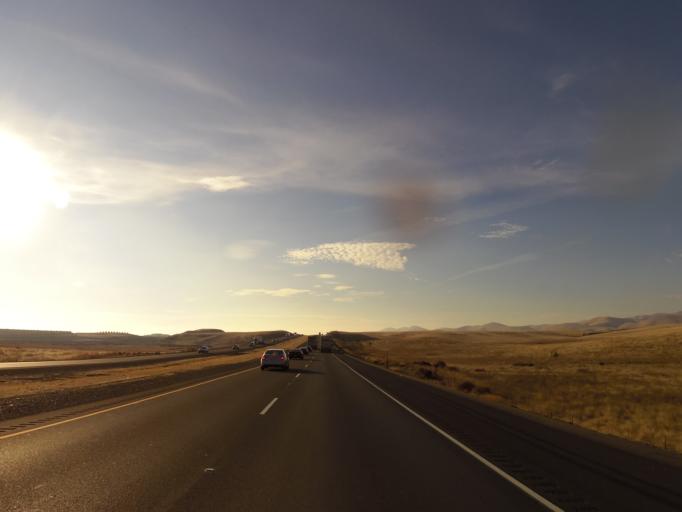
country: US
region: California
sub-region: Stanislaus County
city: Newman
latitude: 37.2726
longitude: -121.0959
